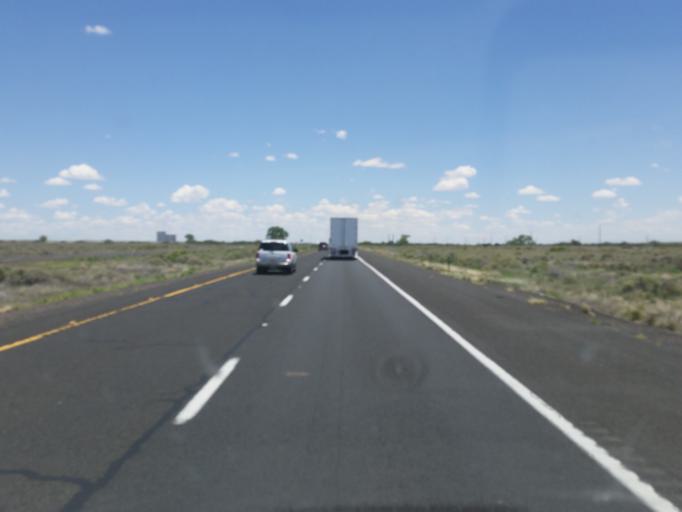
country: US
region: Arizona
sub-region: Navajo County
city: Joseph City
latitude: 34.9661
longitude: -110.4148
